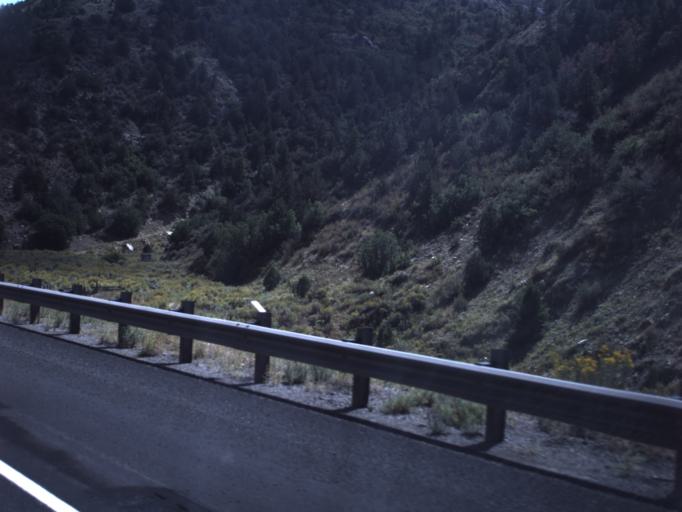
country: US
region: Utah
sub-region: Sevier County
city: Salina
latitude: 38.8822
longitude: -111.5932
